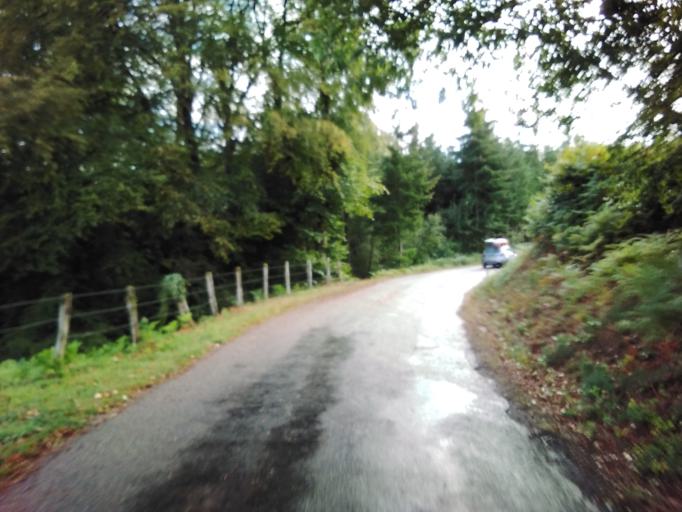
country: FR
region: Bourgogne
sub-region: Departement de la Nievre
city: Lormes
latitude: 47.3005
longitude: 3.8910
